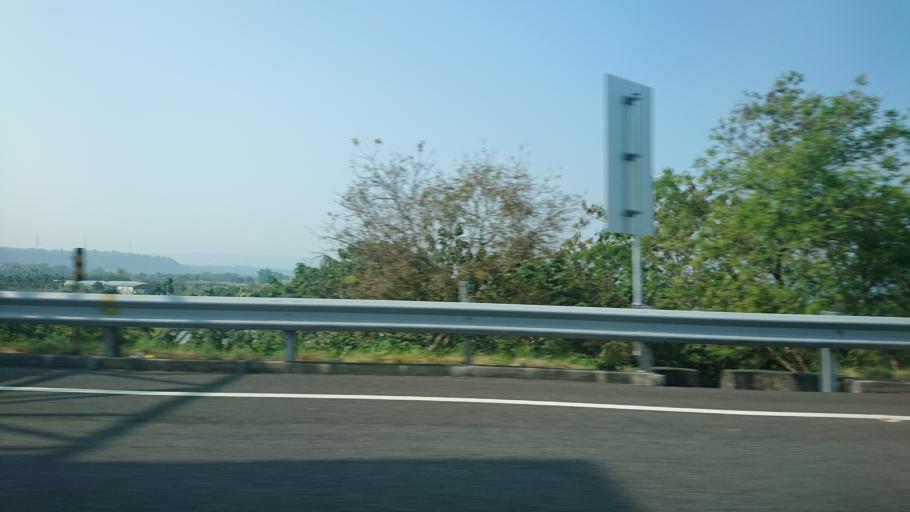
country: TW
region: Taiwan
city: Lugu
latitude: 23.7999
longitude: 120.7000
